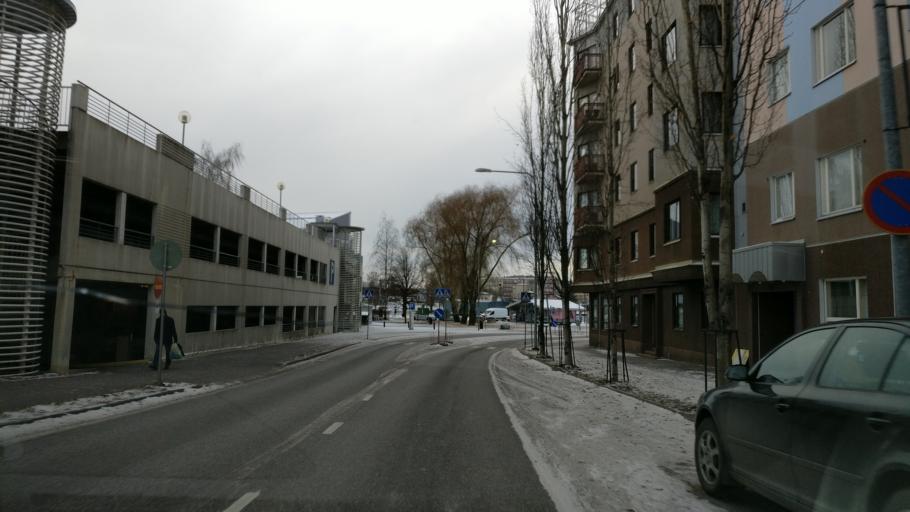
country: FI
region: Southern Savonia
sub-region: Savonlinna
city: Savonlinna
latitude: 61.8662
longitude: 28.8897
